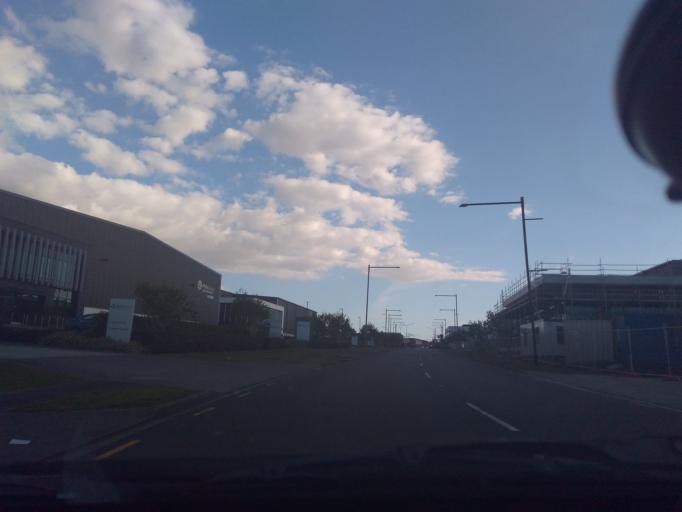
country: NZ
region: Auckland
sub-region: Auckland
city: Tamaki
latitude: -36.9338
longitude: 174.8766
